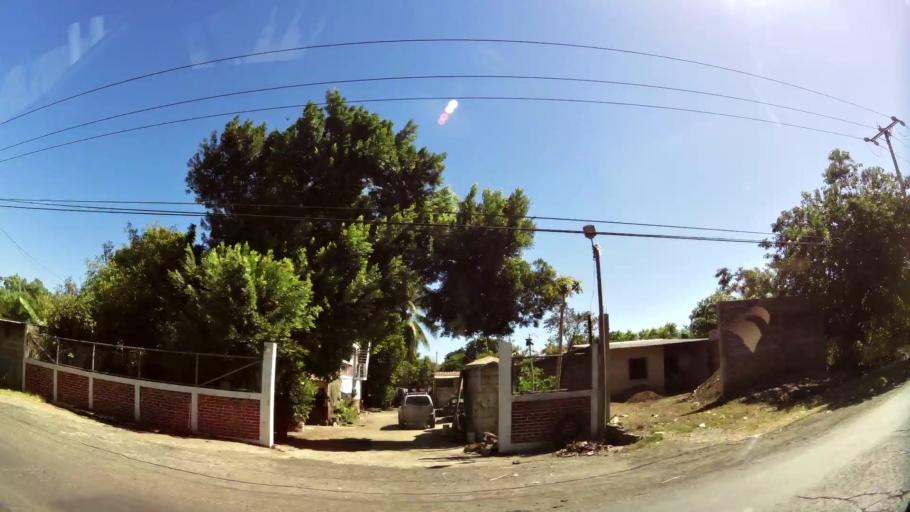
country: SV
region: La Libertad
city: San Juan Opico
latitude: 13.8605
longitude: -89.3595
